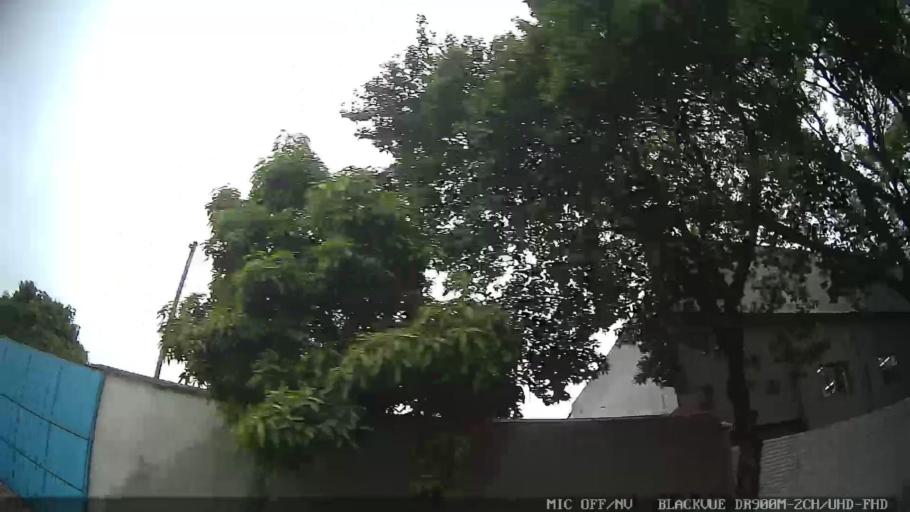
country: BR
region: Sao Paulo
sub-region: Sao Paulo
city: Sao Paulo
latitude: -23.5134
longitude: -46.6970
